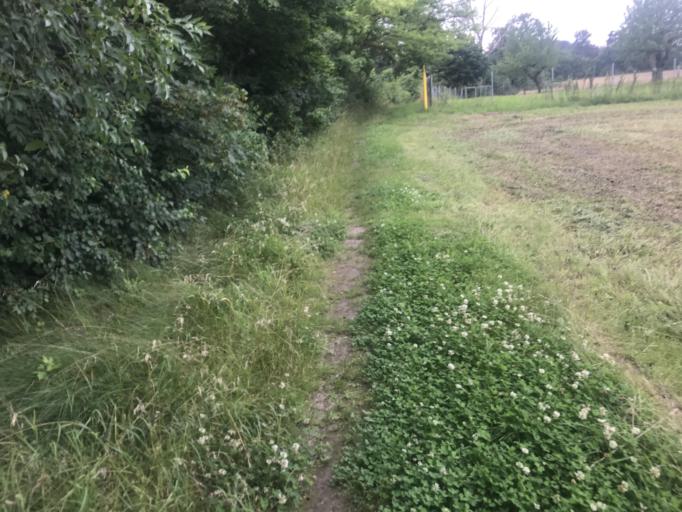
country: DE
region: Saxony-Anhalt
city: Quedlinburg
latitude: 51.7986
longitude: 11.1495
